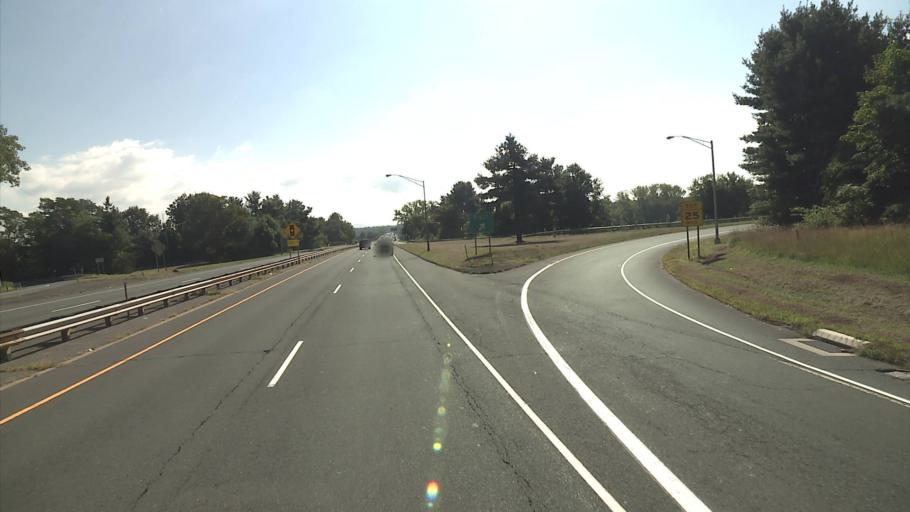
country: US
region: Connecticut
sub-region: Hartford County
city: Thompsonville
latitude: 41.9903
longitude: -72.5903
